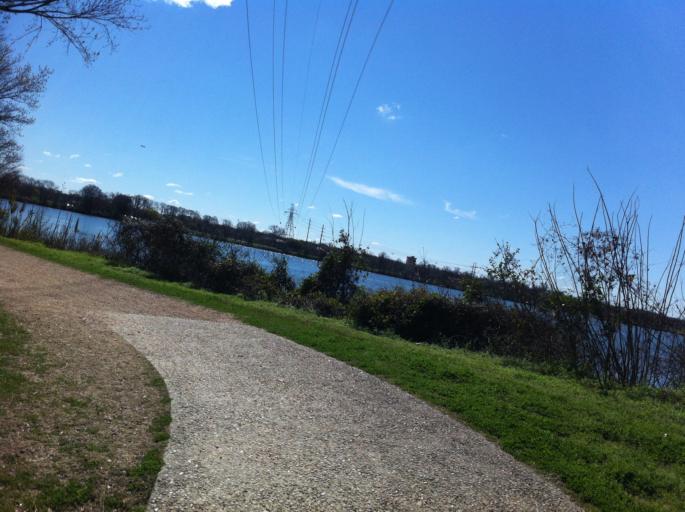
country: US
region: Texas
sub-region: Travis County
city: Austin
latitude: 30.2507
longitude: -97.7186
